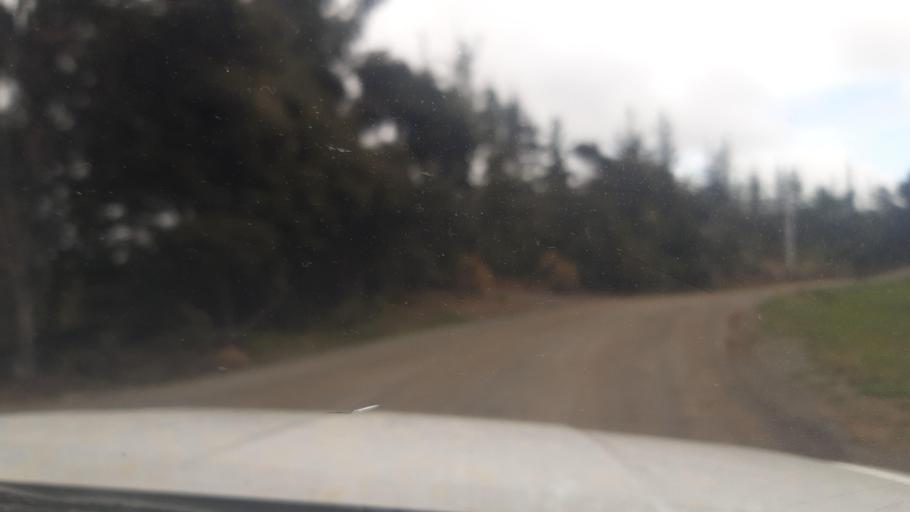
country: NZ
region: Northland
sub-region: Far North District
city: Taipa
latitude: -35.0571
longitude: 173.5380
